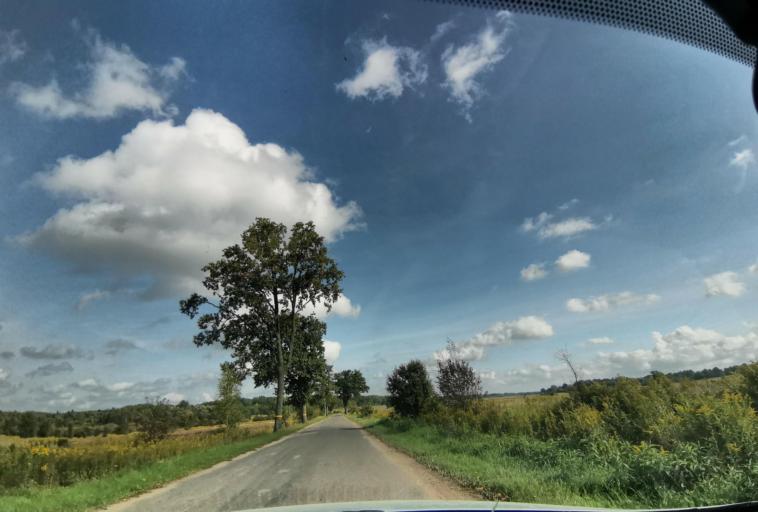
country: RU
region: Kaliningrad
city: Chernyakhovsk
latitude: 54.6635
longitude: 21.9572
